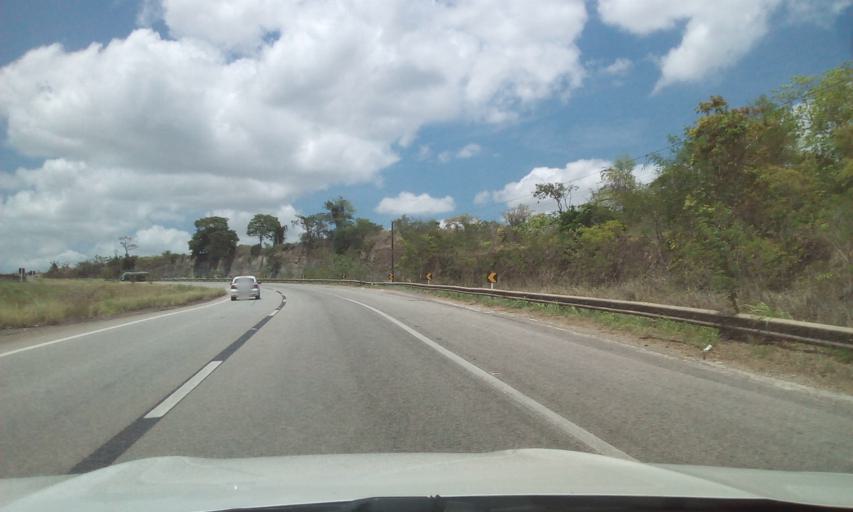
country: BR
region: Alagoas
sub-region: Junqueiro
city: Junqueiro
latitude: -9.8956
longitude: -36.4105
